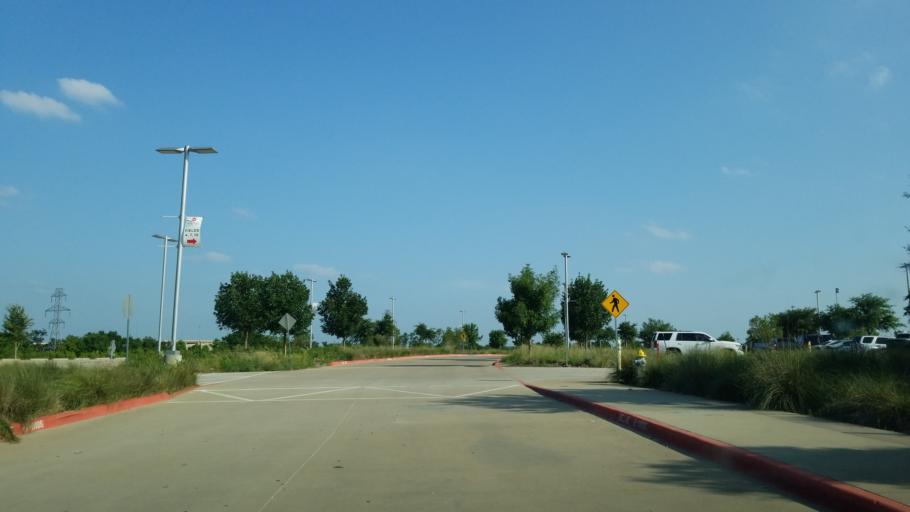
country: US
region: Texas
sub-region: Dallas County
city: Farmers Branch
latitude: 32.8800
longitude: -96.9052
